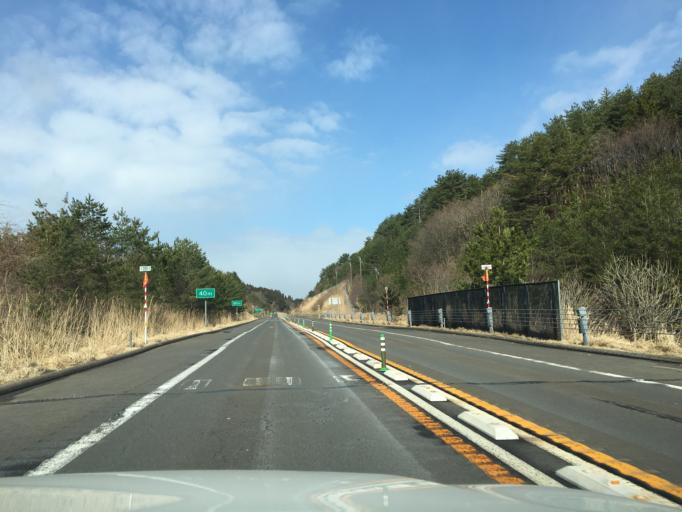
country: JP
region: Akita
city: Akita
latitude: 39.7612
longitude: 140.1298
